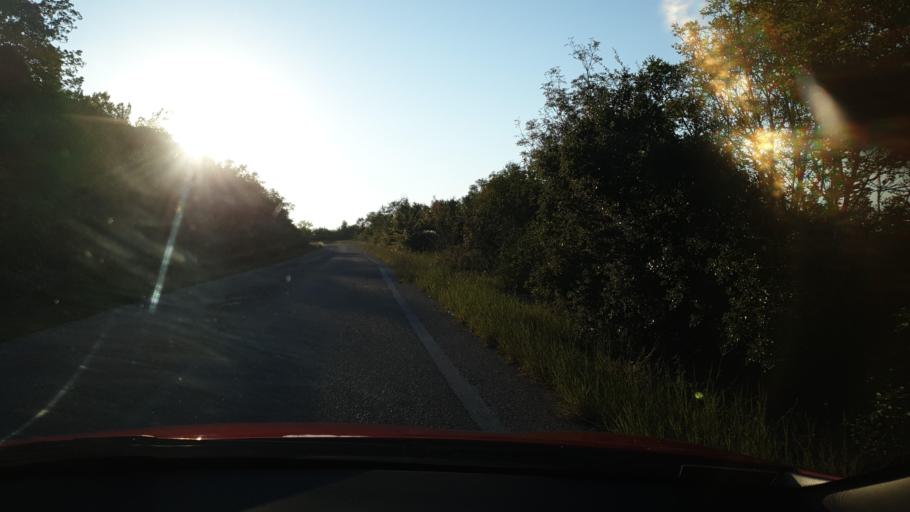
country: GR
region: Central Macedonia
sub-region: Nomos Chalkidikis
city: Galatista
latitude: 40.5522
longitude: 23.2867
